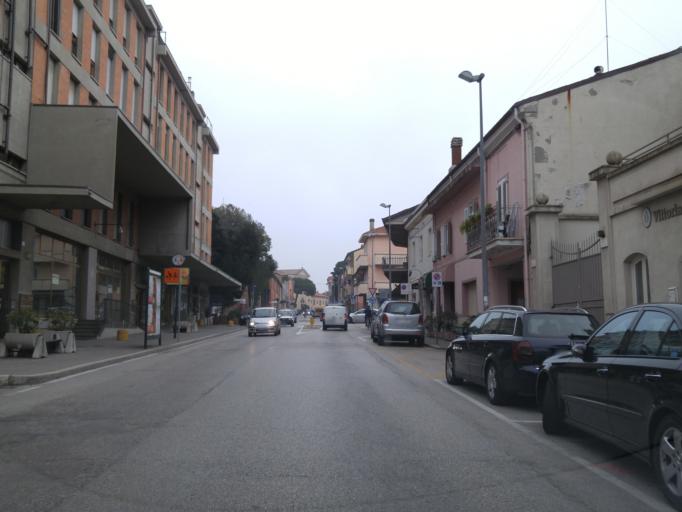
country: IT
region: Emilia-Romagna
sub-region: Provincia di Rimini
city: Cattolica
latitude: 43.9630
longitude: 12.7403
